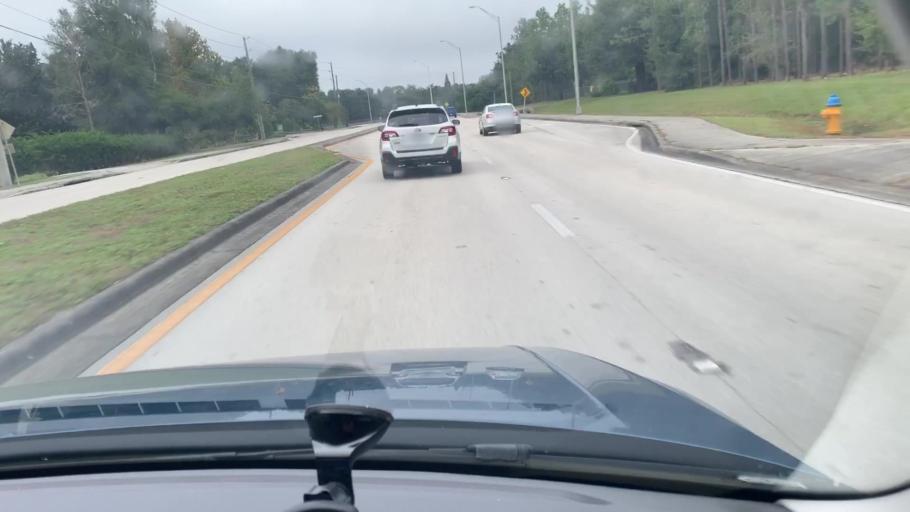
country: US
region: Florida
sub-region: Polk County
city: Gibsonia
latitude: 28.0934
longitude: -81.9974
